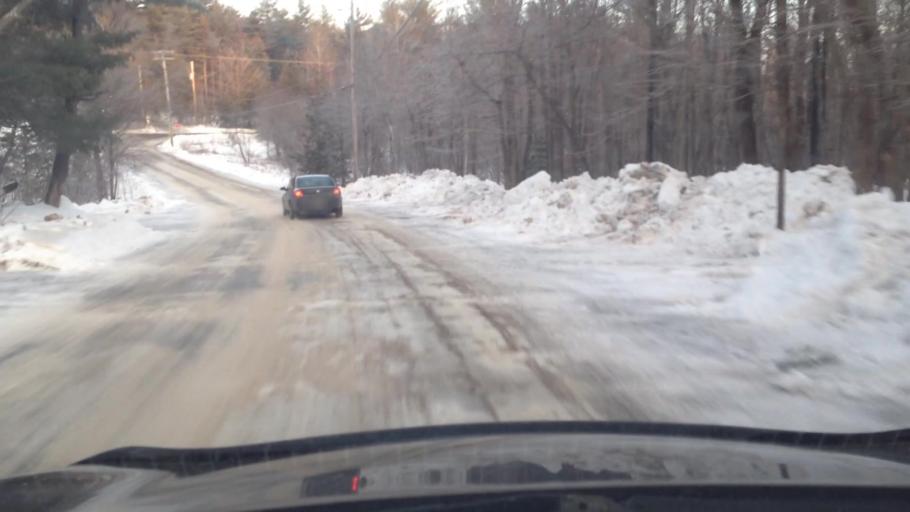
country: CA
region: Quebec
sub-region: Lanaudiere
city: Sainte-Julienne
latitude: 45.9532
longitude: -73.7561
